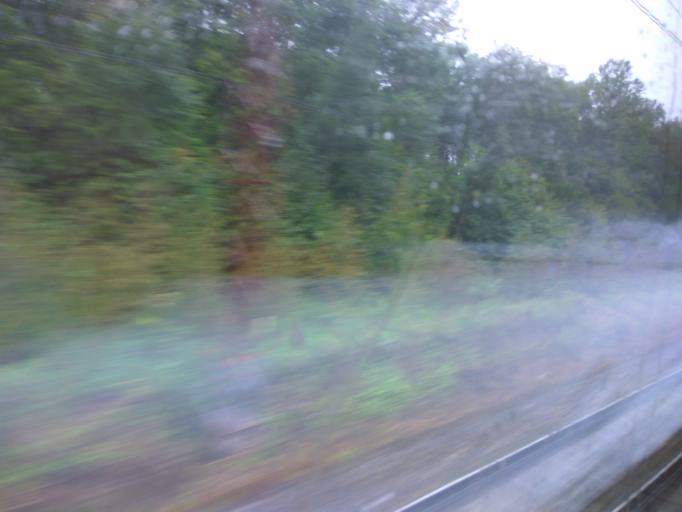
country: RU
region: Moskovskaya
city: Zhilevo
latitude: 55.0252
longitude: 38.0107
